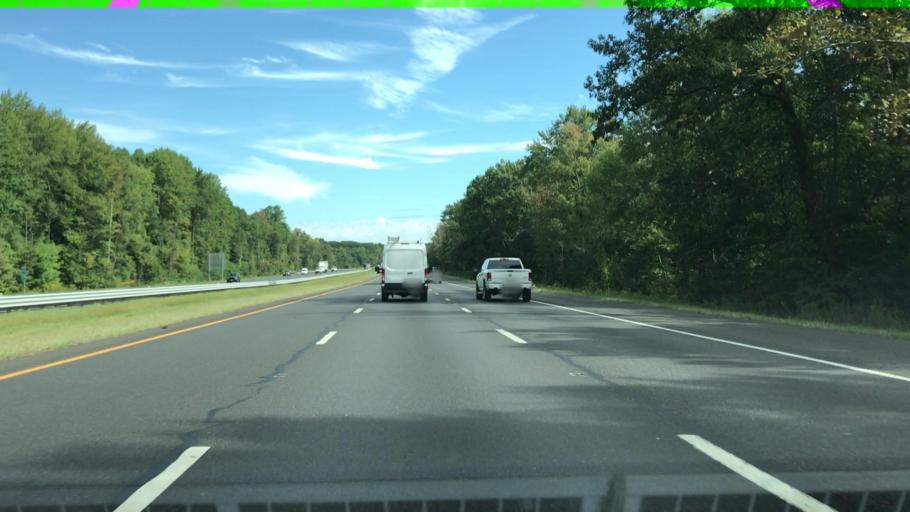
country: US
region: New Jersey
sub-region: Burlington County
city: Burlington
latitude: 40.0553
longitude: -74.8198
